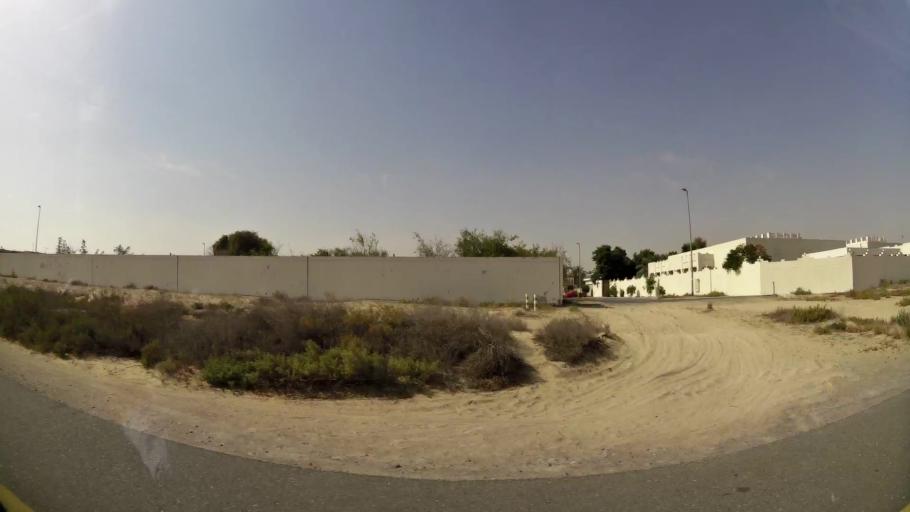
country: AE
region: Ash Shariqah
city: Sharjah
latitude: 25.2542
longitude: 55.4240
